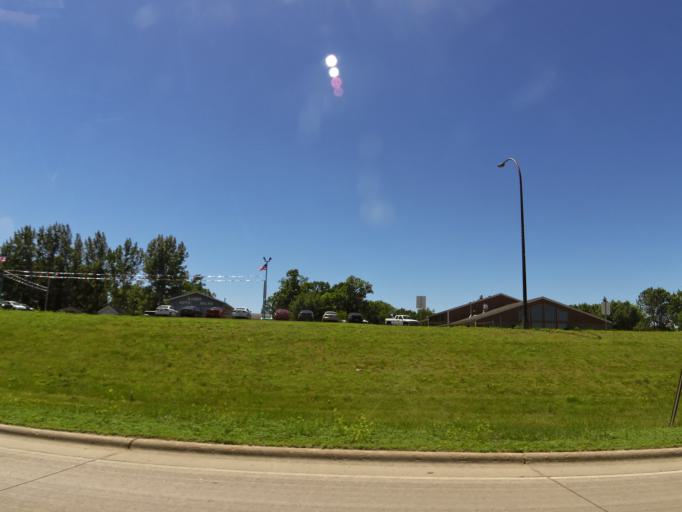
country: US
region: Minnesota
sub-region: Becker County
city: Detroit Lakes
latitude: 46.8107
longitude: -95.8259
